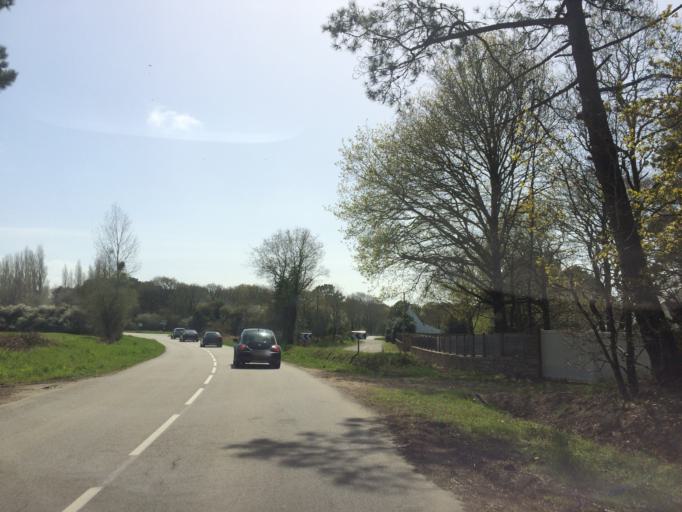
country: FR
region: Brittany
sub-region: Departement du Morbihan
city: Ploemel
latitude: 47.6189
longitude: -3.0551
